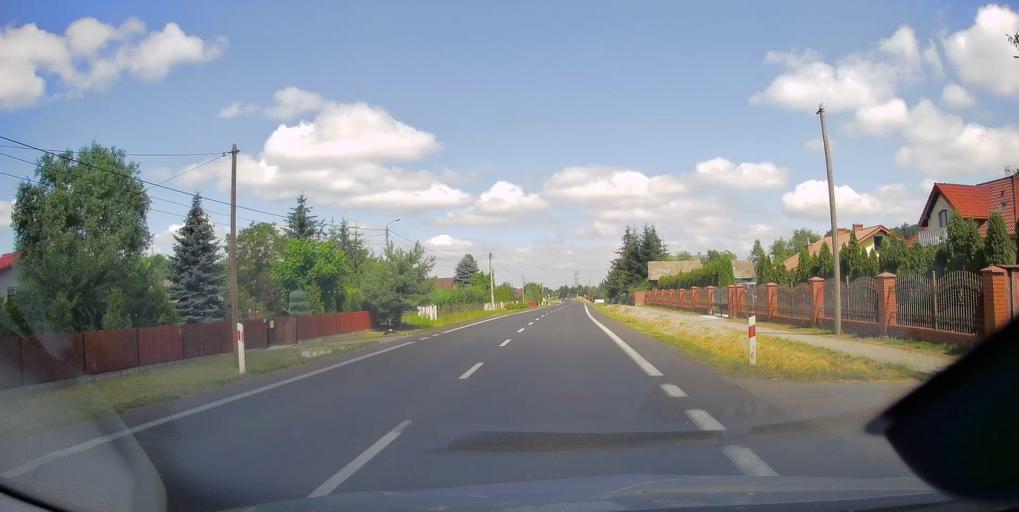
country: PL
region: Subcarpathian Voivodeship
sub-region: Powiat debicki
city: Brzeznica
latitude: 50.1185
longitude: 21.4893
